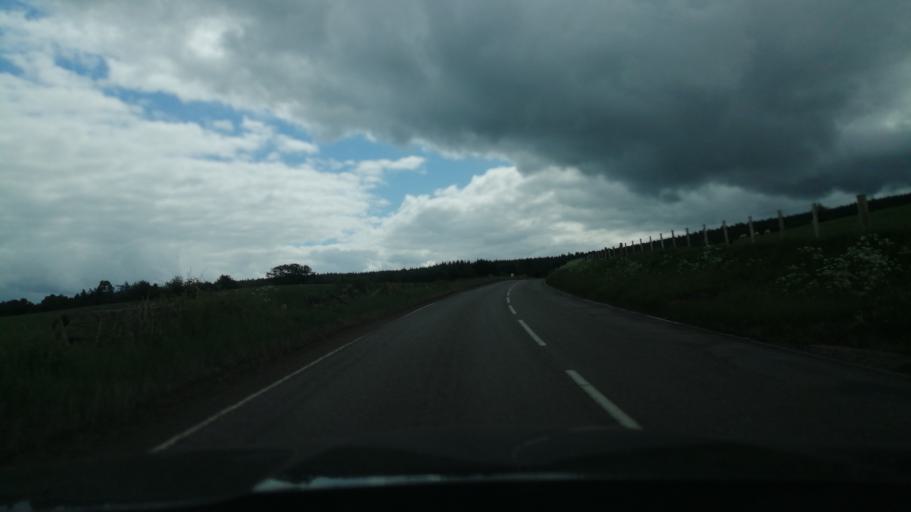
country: GB
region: Scotland
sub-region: Moray
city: Fochabers
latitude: 57.5488
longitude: -3.1284
